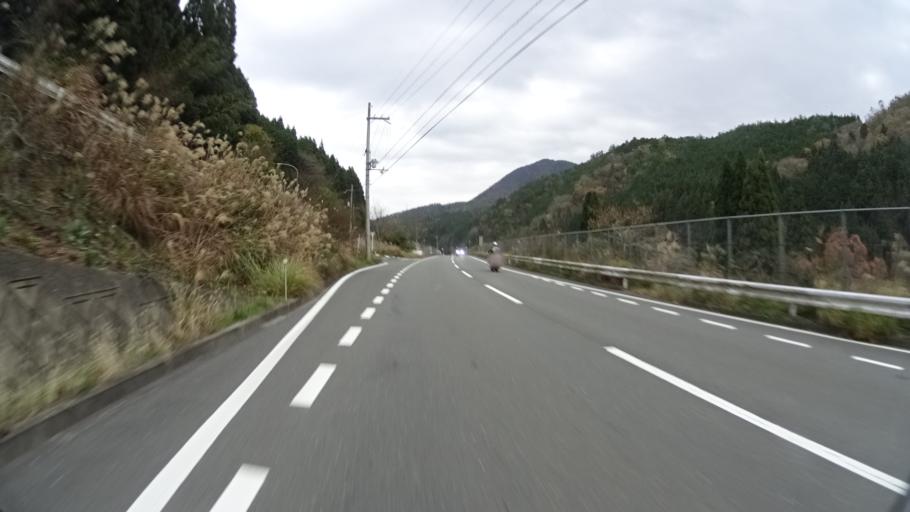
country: JP
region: Hyogo
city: Sasayama
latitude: 35.0681
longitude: 135.3926
